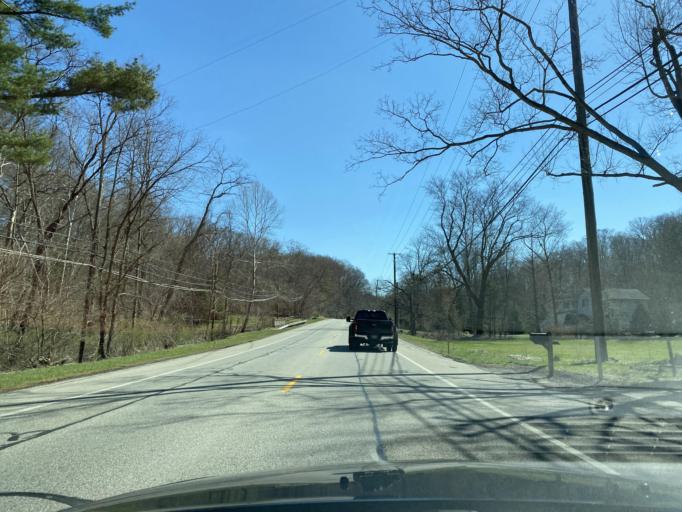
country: US
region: Ohio
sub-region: Summit County
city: Montrose-Ghent
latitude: 41.1640
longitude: -81.6369
